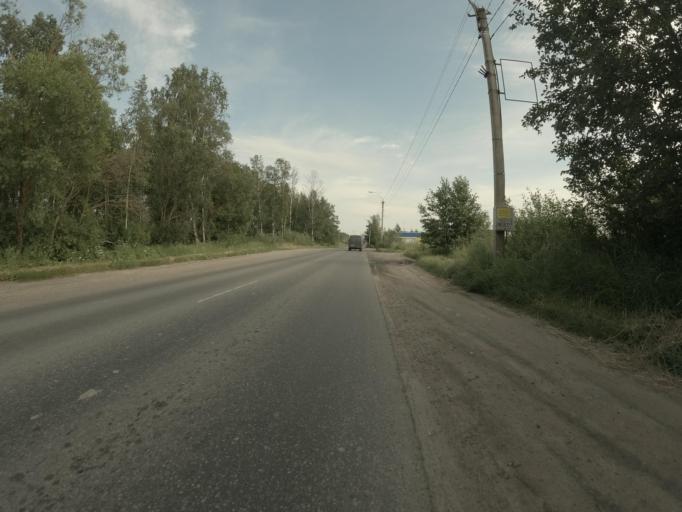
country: RU
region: St.-Petersburg
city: Krasnogvargeisky
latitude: 59.9346
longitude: 30.5204
